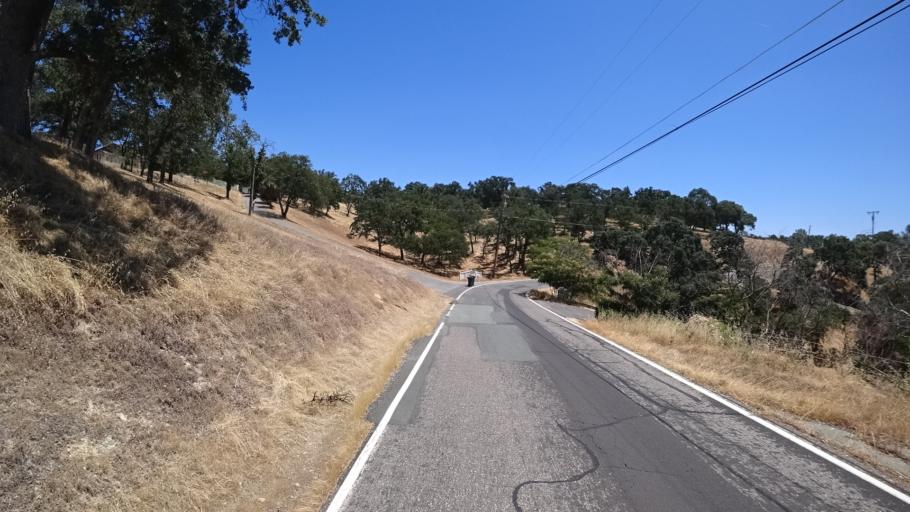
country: US
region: California
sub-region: Calaveras County
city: Rancho Calaveras
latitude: 38.1368
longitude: -120.8602
